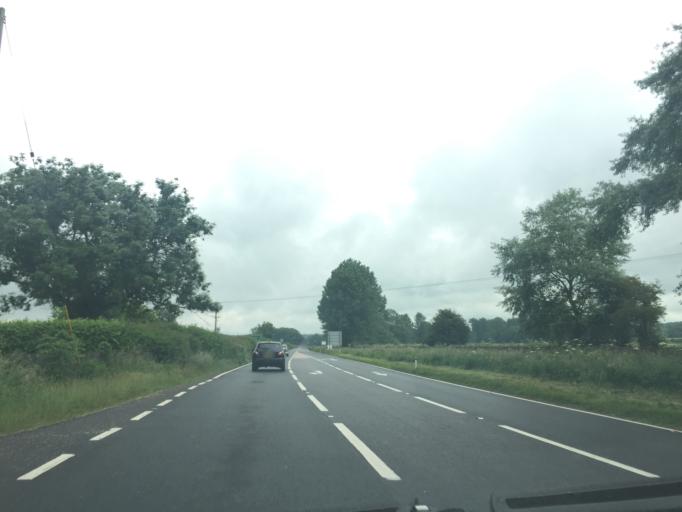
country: GB
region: England
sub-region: Dorset
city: Lytchett Matravers
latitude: 50.7823
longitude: -2.1319
